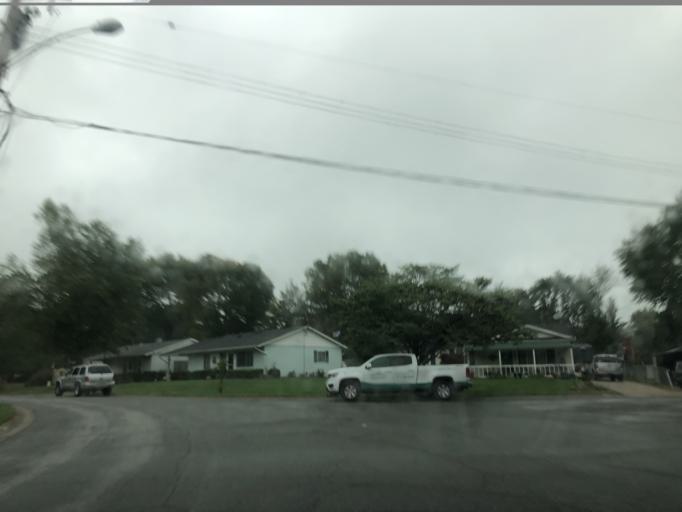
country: US
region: Ohio
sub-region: Hamilton County
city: Loveland
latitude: 39.2661
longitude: -84.2759
